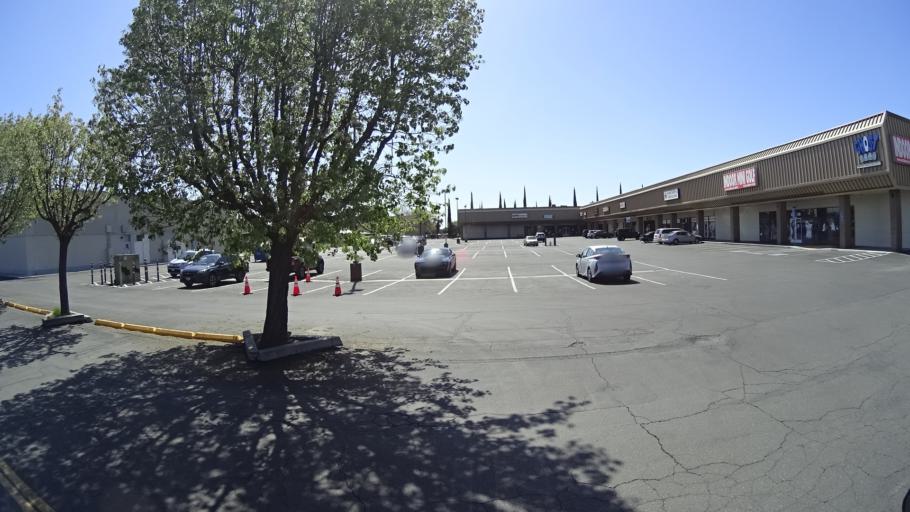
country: US
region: California
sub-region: Fresno County
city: Fresno
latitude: 36.8122
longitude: -119.7916
